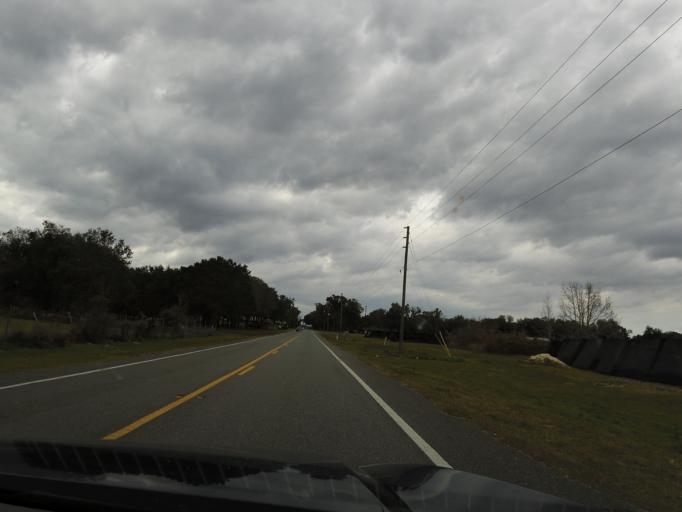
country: US
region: Florida
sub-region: Putnam County
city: Crescent City
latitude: 29.3332
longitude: -81.4970
